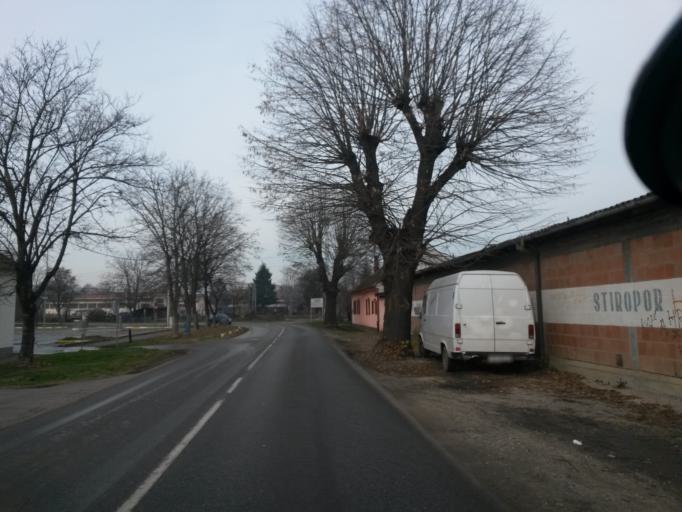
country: HR
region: Vukovarsko-Srijemska
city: Vinkovci
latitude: 45.3006
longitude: 18.8102
